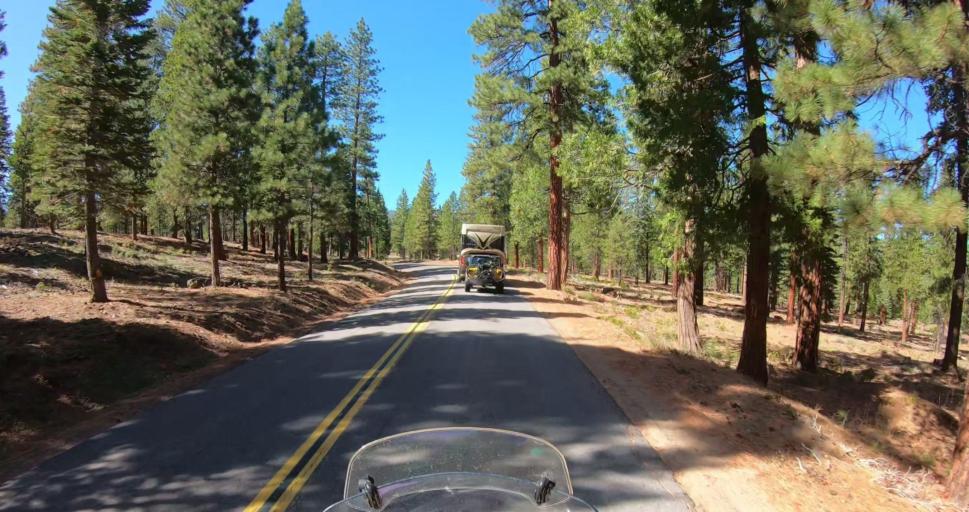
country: US
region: California
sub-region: Lassen County
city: Susanville
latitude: 40.4452
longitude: -120.7559
